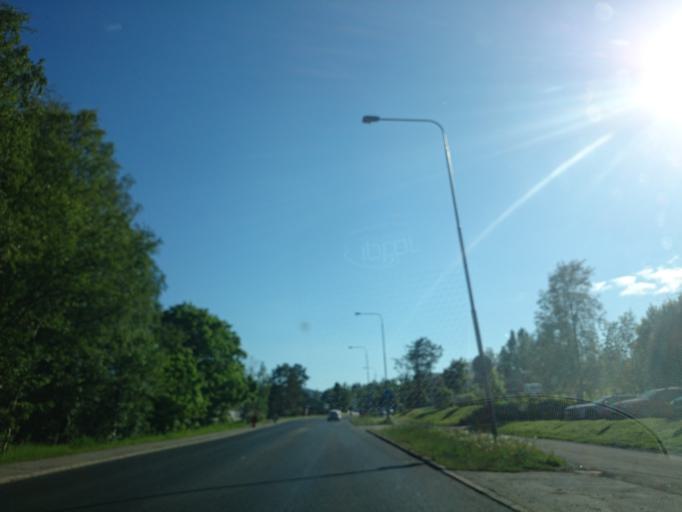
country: SE
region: Vaesternorrland
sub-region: Haernoesands Kommun
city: Haernoesand
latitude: 62.6212
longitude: 17.9156
